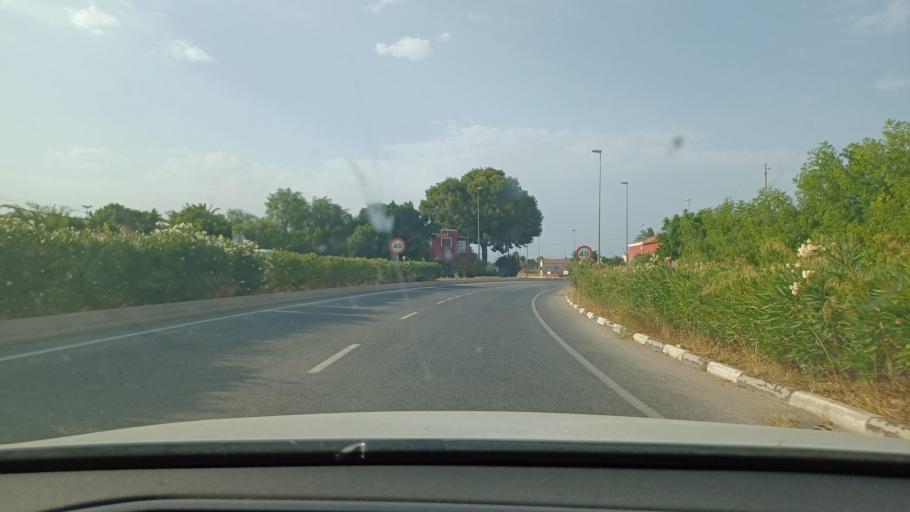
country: ES
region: Valencia
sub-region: Provincia de Alicante
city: Elche
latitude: 38.2132
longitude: -0.6976
